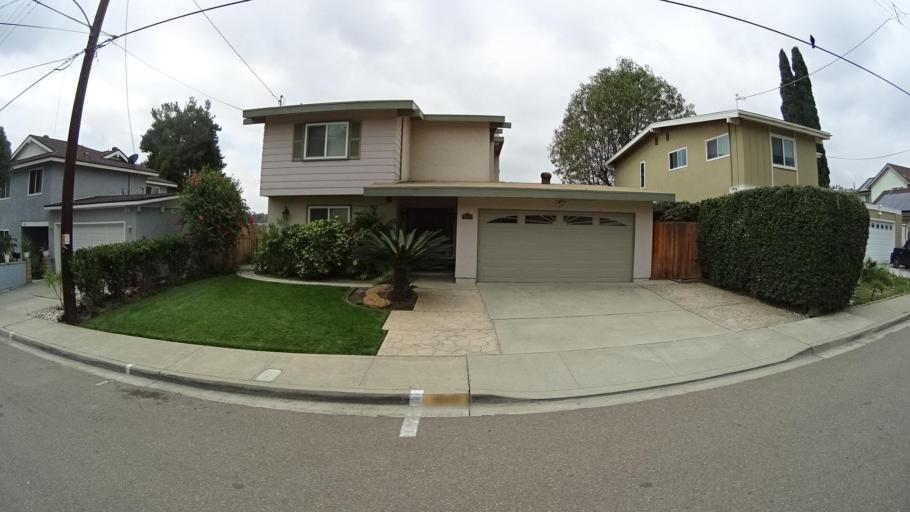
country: US
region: California
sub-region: San Diego County
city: Spring Valley
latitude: 32.7483
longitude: -117.0111
